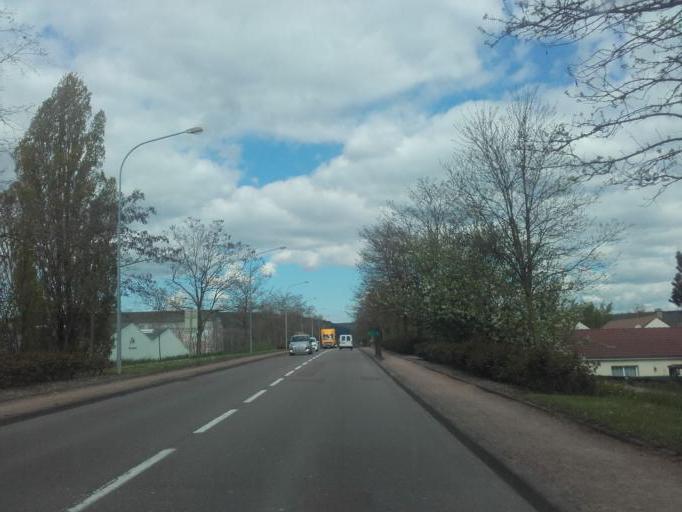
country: FR
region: Bourgogne
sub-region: Departement de la Cote-d'Or
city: Nuits-Saint-Georges
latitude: 47.1338
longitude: 4.9612
